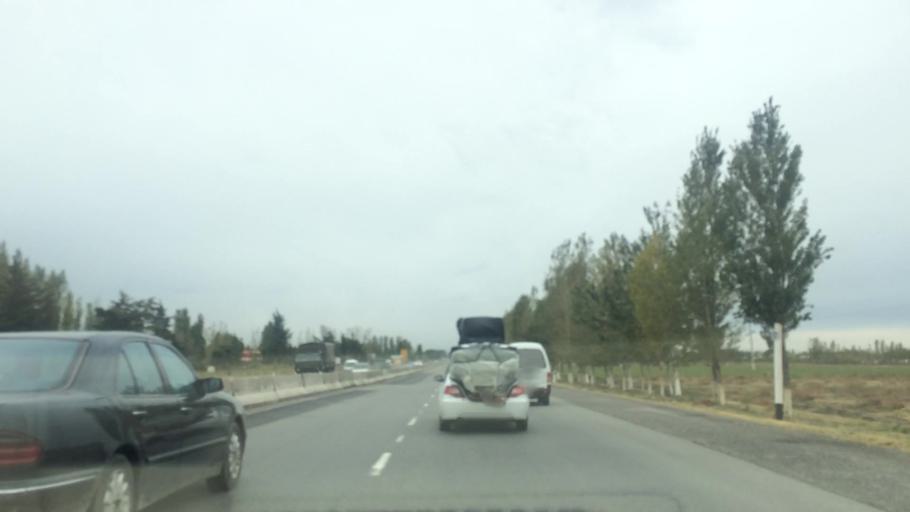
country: UZ
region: Samarqand
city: Bulung'ur
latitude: 39.7881
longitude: 67.3140
